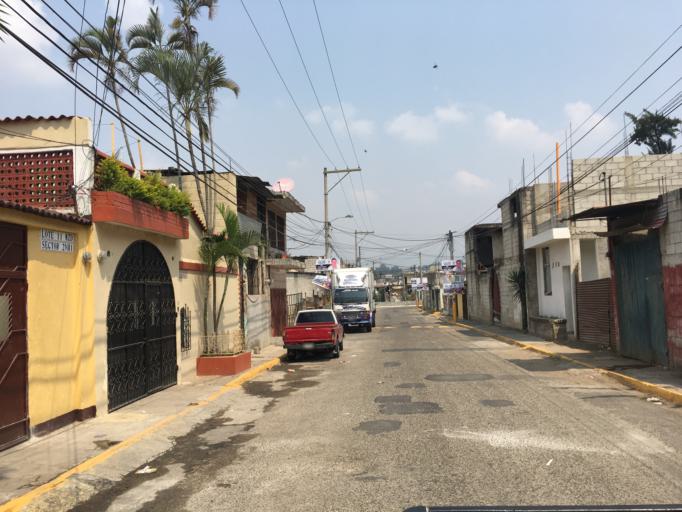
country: GT
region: Guatemala
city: Petapa
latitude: 14.5180
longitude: -90.5406
